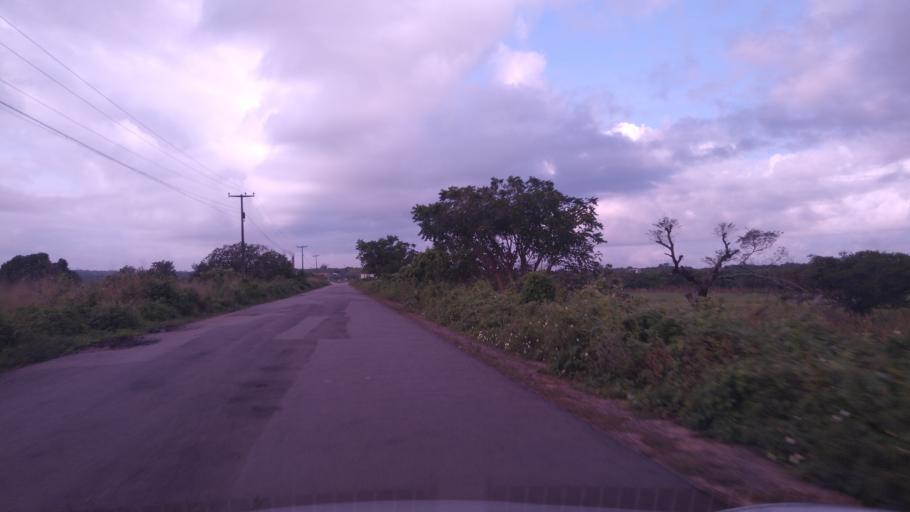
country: BR
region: Ceara
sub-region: Chorozinho
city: Chorozinho
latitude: -4.3081
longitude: -38.4983
